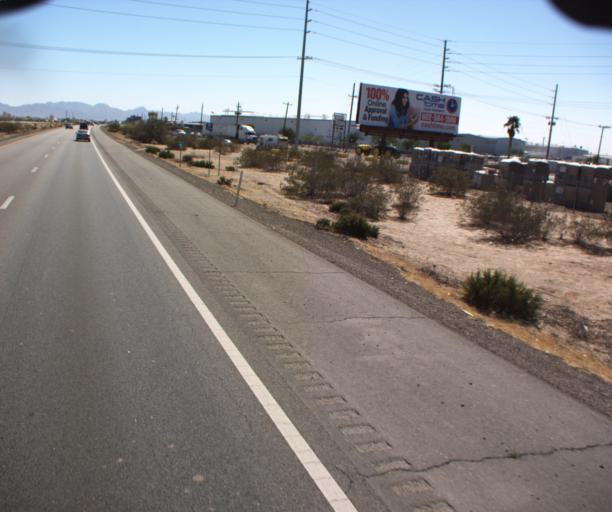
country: US
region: Arizona
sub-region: Yuma County
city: Yuma
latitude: 32.6851
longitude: -114.5651
